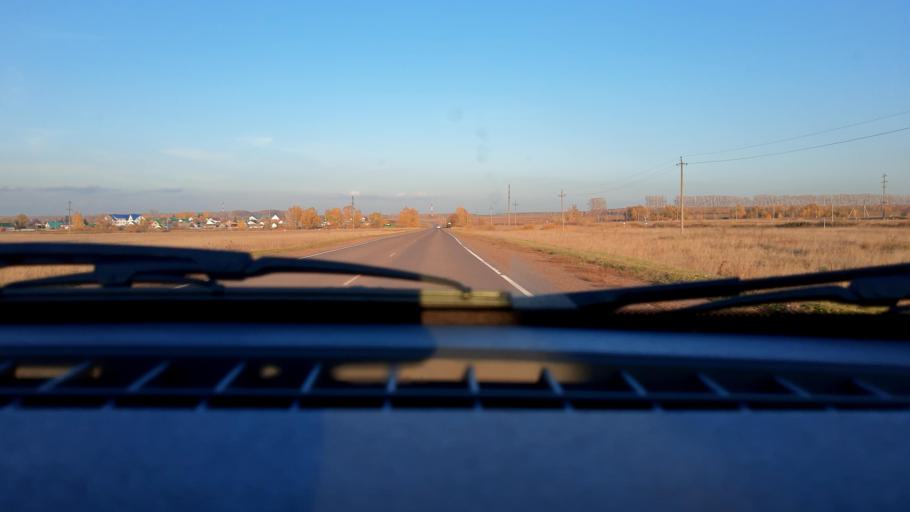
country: RU
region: Bashkortostan
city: Asanovo
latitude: 54.8047
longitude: 55.5524
